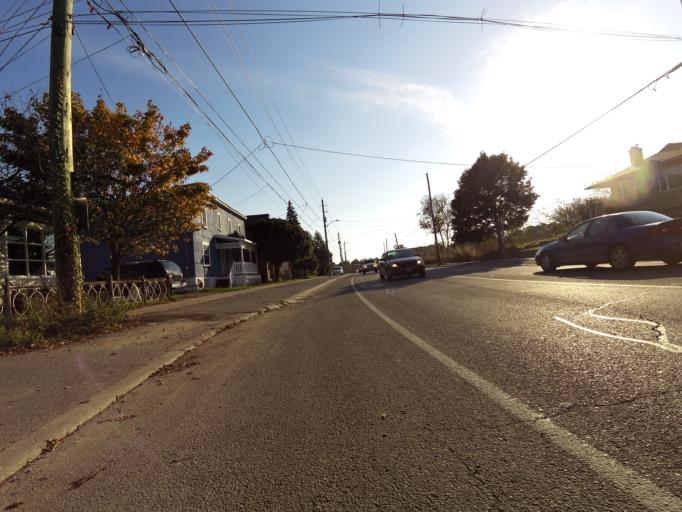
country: CA
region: Ontario
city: Kingston
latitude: 44.2502
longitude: -76.4857
